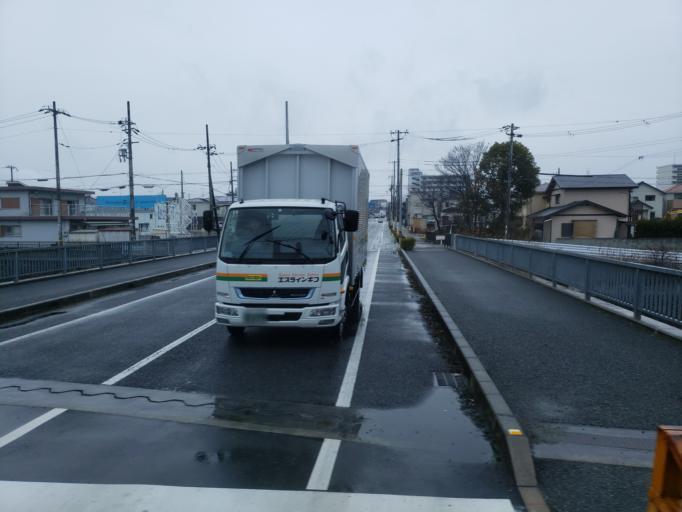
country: JP
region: Hyogo
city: Kakogawacho-honmachi
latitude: 34.6933
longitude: 134.8965
